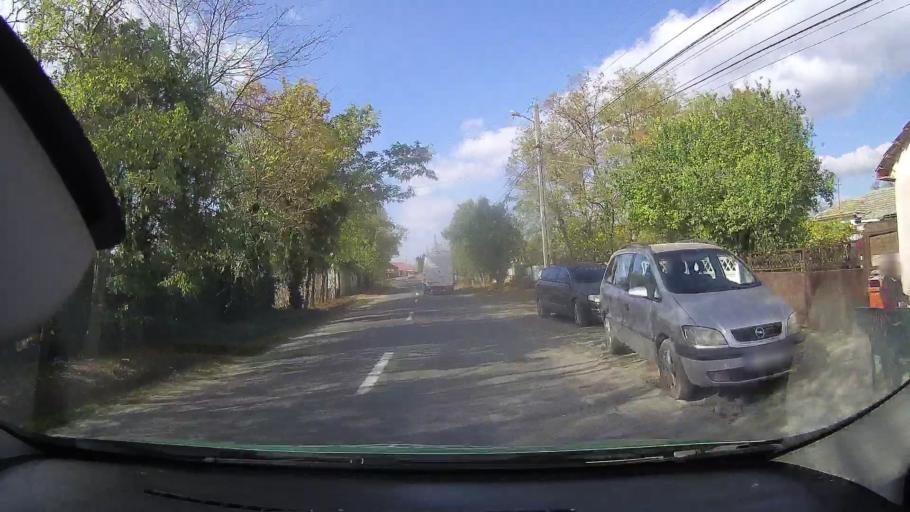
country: RO
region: Constanta
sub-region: Comuna Istria
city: Nuntasi
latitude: 44.5400
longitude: 28.6490
